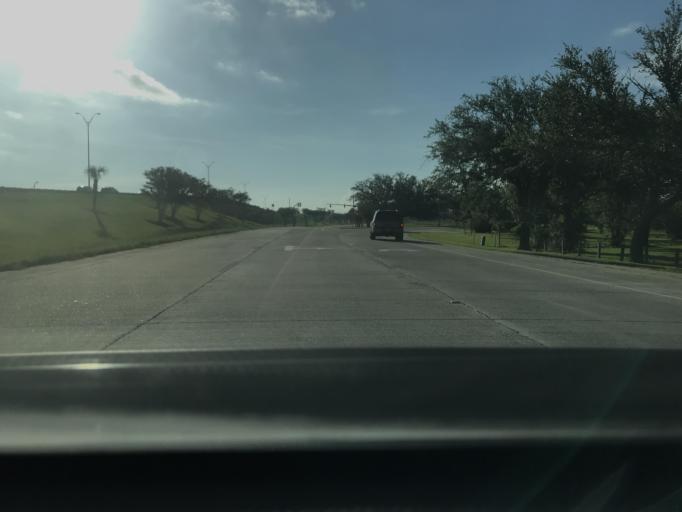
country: US
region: Louisiana
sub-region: Calcasieu Parish
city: Westlake
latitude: 30.2364
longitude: -93.2225
